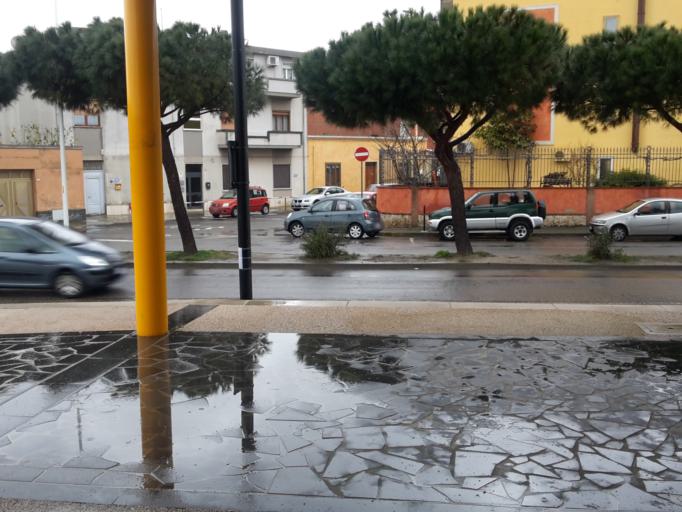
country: IT
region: Sardinia
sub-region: Provincia di Cagliari
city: Monserrato
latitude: 39.2638
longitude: 9.1419
